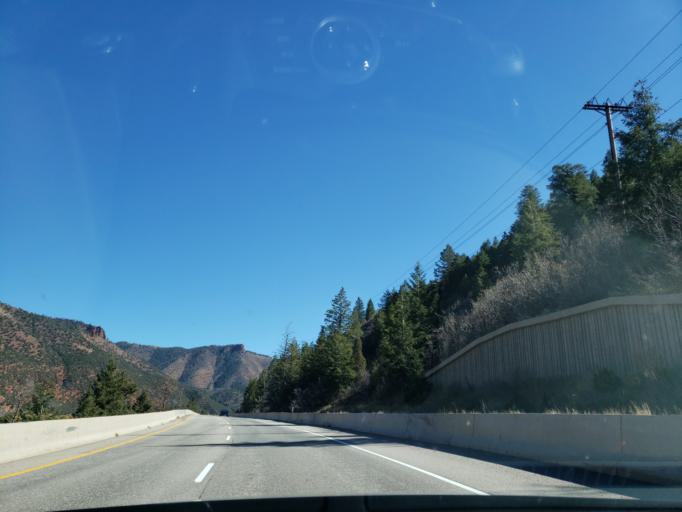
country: US
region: Colorado
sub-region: Eagle County
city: Basalt
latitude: 39.3288
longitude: -106.9704
